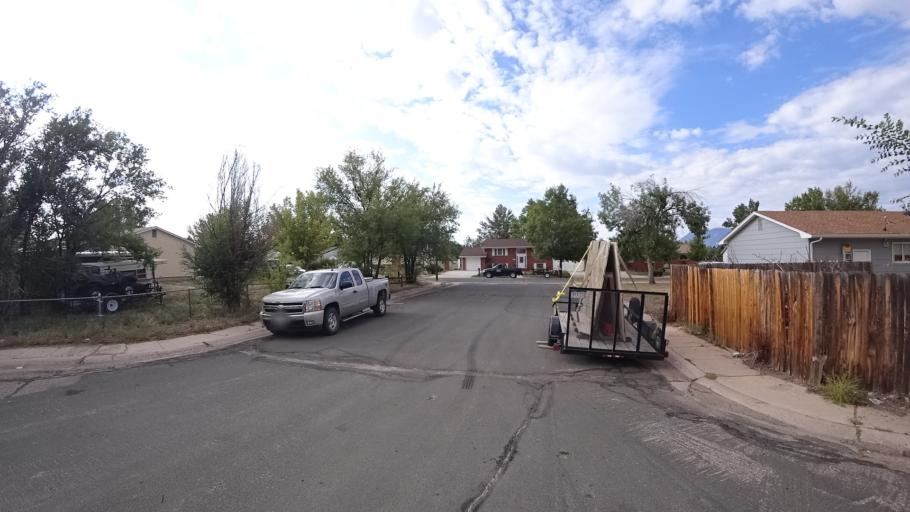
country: US
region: Colorado
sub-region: El Paso County
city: Cimarron Hills
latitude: 38.8465
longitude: -104.7517
